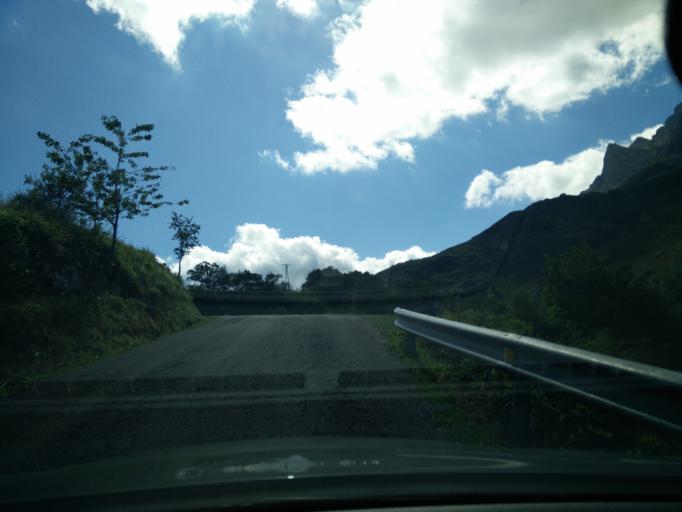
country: ES
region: Castille and Leon
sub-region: Provincia de Leon
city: Posada de Valdeon
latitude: 43.1630
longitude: -4.9103
